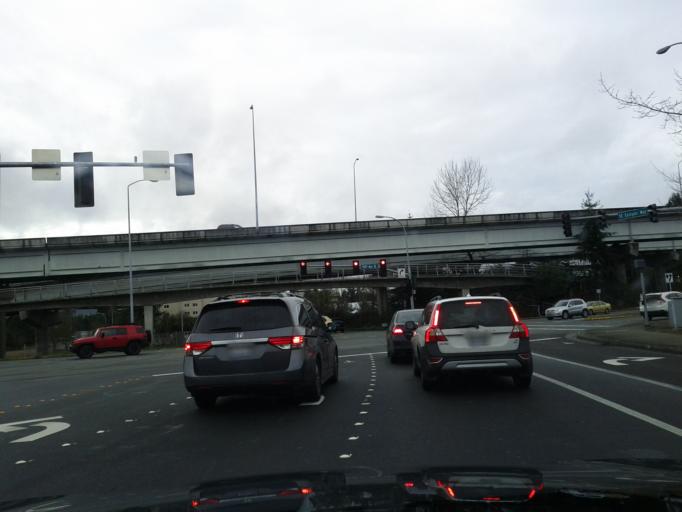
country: US
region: Washington
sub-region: King County
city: Eastgate
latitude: 47.5808
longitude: -122.1407
